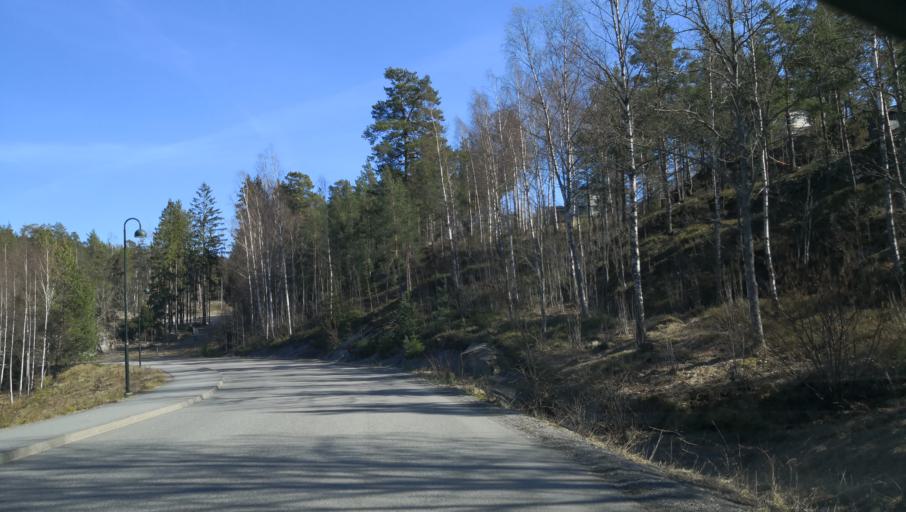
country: SE
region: Stockholm
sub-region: Varmdo Kommun
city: Gustavsberg
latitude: 59.3070
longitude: 18.3542
